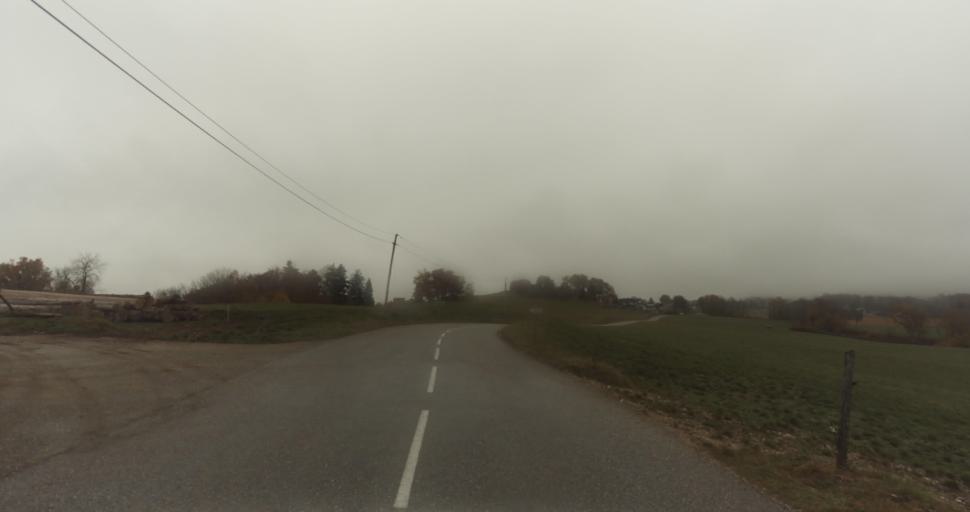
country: FR
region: Rhone-Alpes
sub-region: Departement de la Haute-Savoie
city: Saint-Martin-Bellevue
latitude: 45.9688
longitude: 6.1723
